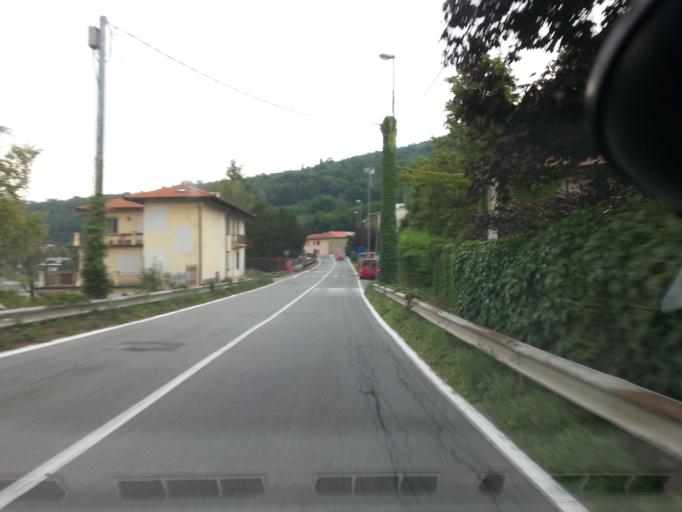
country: IT
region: Piedmont
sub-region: Provincia di Torino
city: Avigliana
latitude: 45.0610
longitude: 7.3903
